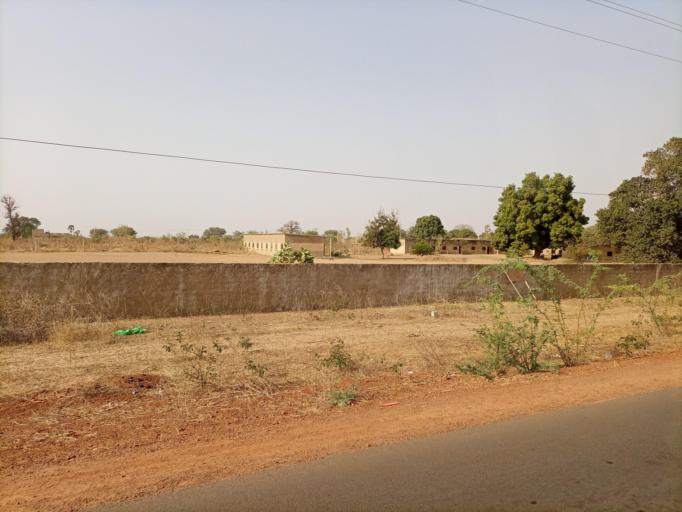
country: SN
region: Fatick
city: Foundiougne
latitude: 14.1207
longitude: -16.4412
